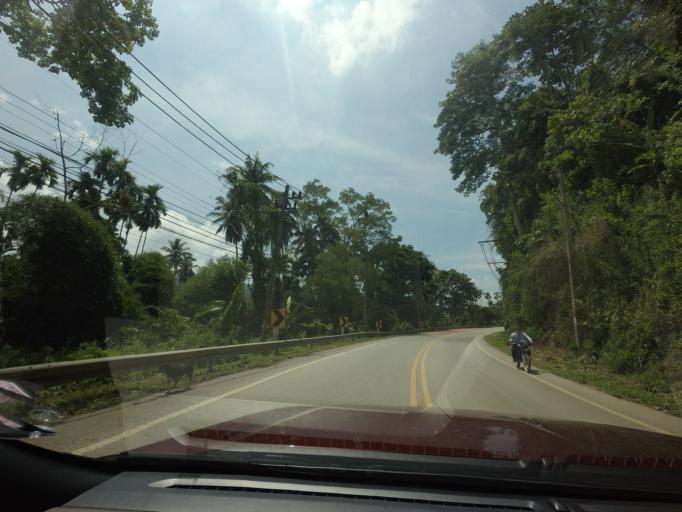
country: TH
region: Yala
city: Betong
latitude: 5.8150
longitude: 101.0856
